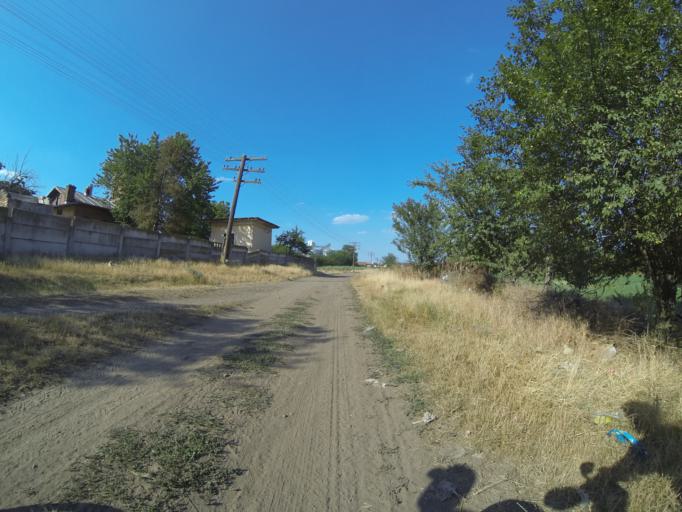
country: RO
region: Dolj
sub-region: Comuna Segarcea
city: Segarcea
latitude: 44.0814
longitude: 23.7254
